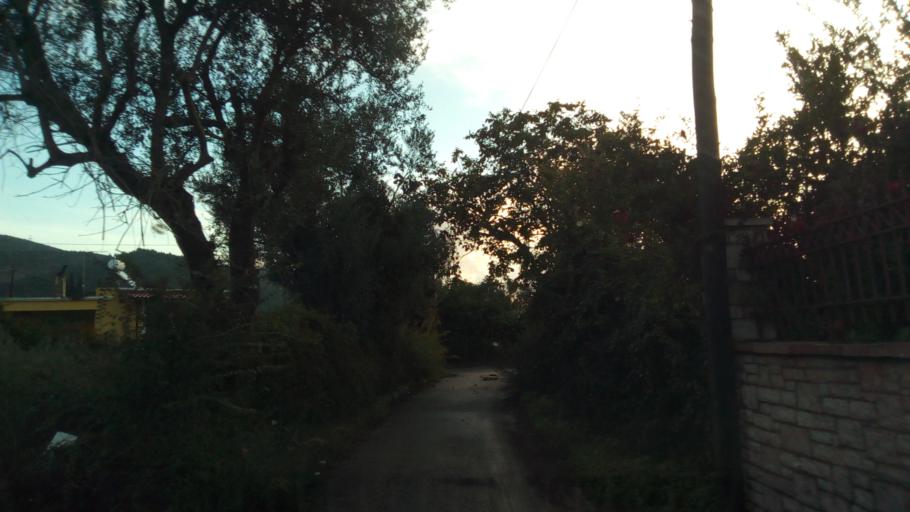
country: GR
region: West Greece
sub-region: Nomos Aitolias kai Akarnanias
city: Nafpaktos
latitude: 38.3900
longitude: 21.8052
